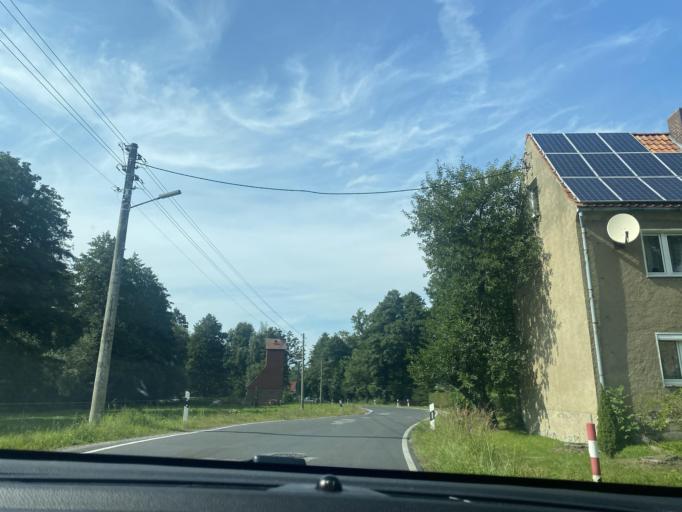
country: DE
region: Saxony
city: Sohland am Rotstein
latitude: 51.1251
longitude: 14.7834
